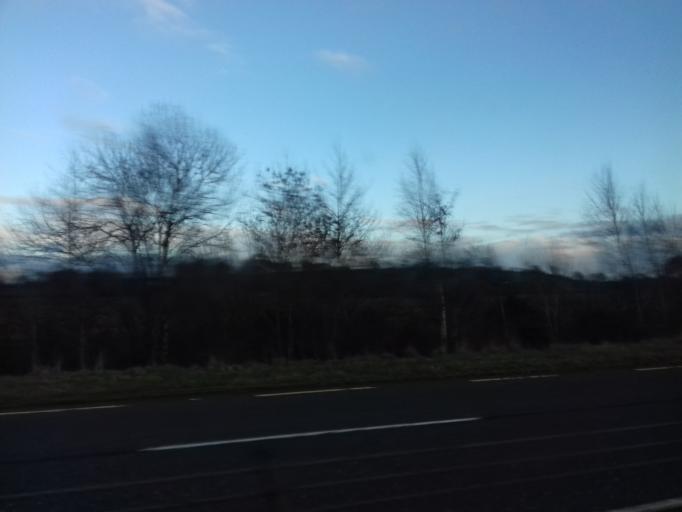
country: IE
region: Ulster
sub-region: County Monaghan
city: Castleblayney
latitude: 54.1762
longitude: -6.8146
